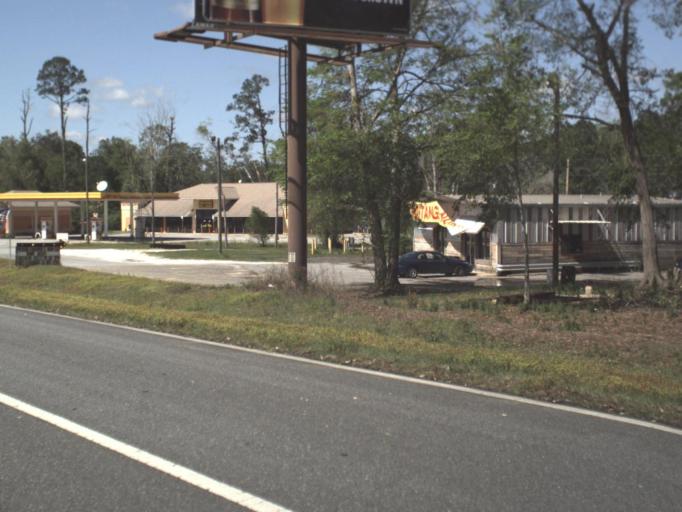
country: US
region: Florida
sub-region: Escambia County
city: Cantonment
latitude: 30.6170
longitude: -87.3239
